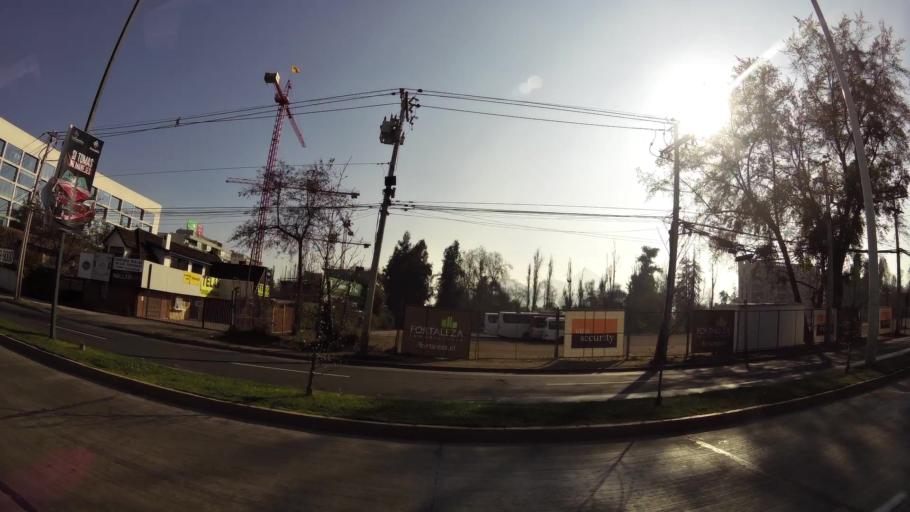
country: CL
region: Santiago Metropolitan
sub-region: Provincia de Santiago
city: Villa Presidente Frei, Nunoa, Santiago, Chile
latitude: -33.3542
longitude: -70.5181
